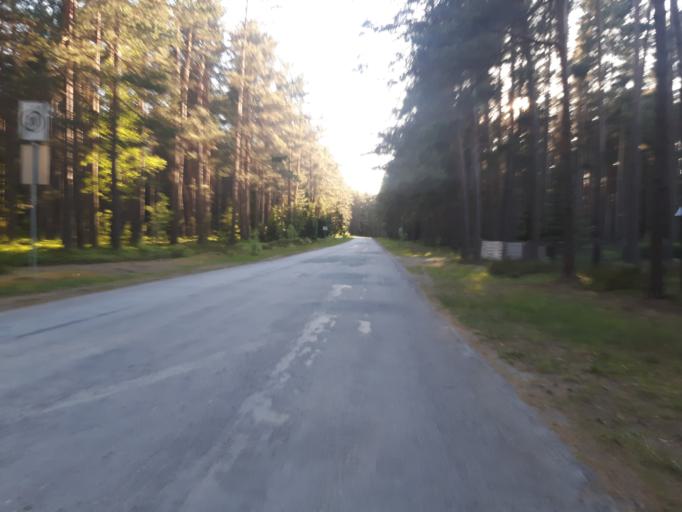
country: EE
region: Harju
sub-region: Loksa linn
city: Loksa
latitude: 59.5747
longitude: 25.9512
